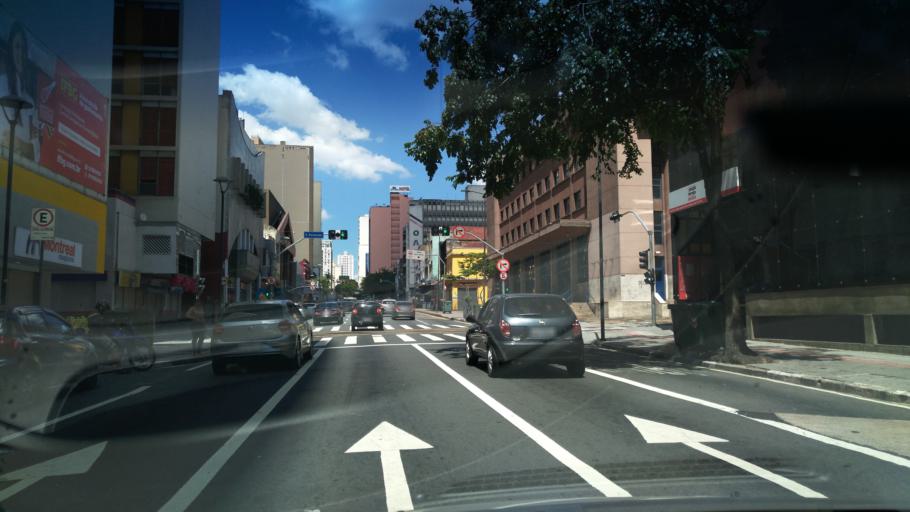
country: BR
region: Sao Paulo
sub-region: Campinas
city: Campinas
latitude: -22.9061
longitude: -47.0591
